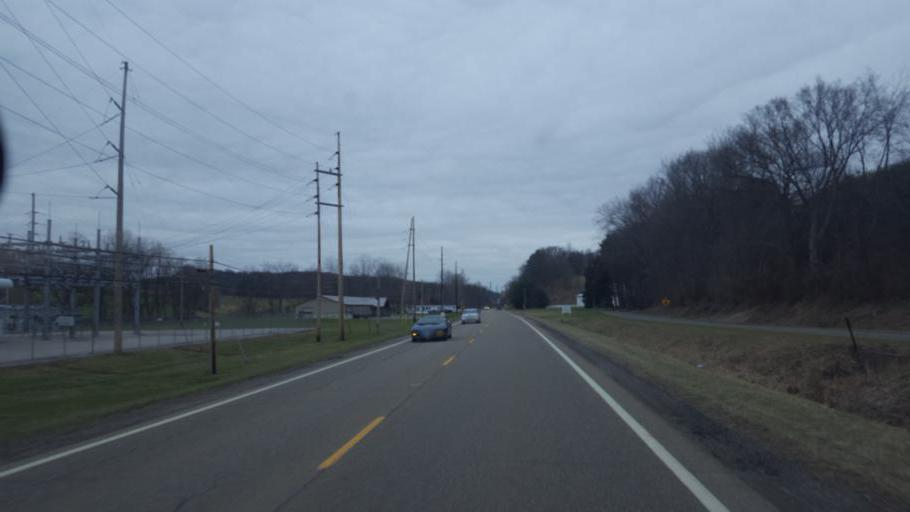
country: US
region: Ohio
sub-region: Holmes County
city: Millersburg
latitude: 40.5619
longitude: -81.9484
